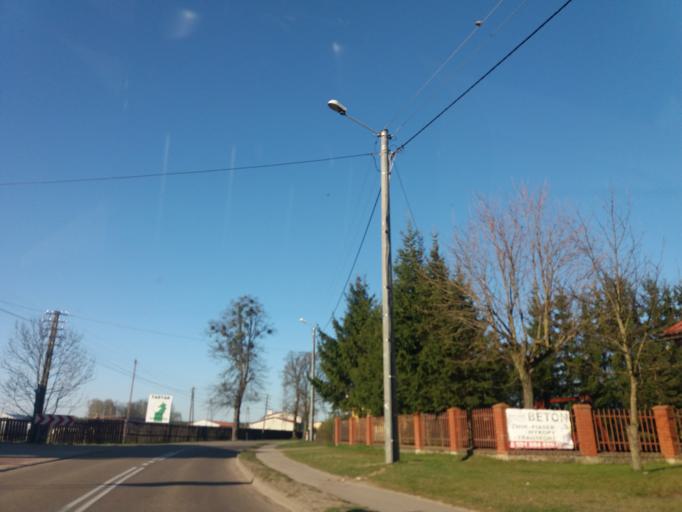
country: PL
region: Warmian-Masurian Voivodeship
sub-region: Powiat nidzicki
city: Nidzica
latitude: 53.4078
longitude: 20.4856
